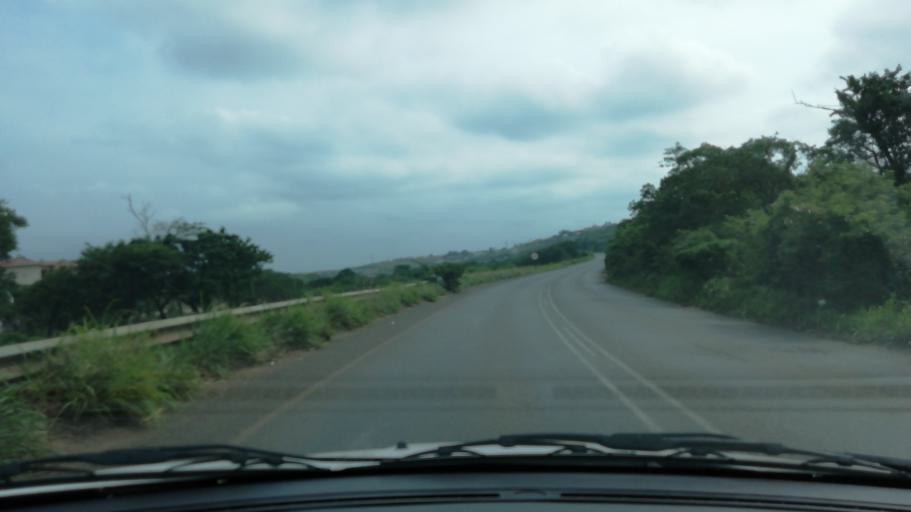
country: ZA
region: KwaZulu-Natal
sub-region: uThungulu District Municipality
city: Empangeni
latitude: -28.7489
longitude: 31.8800
